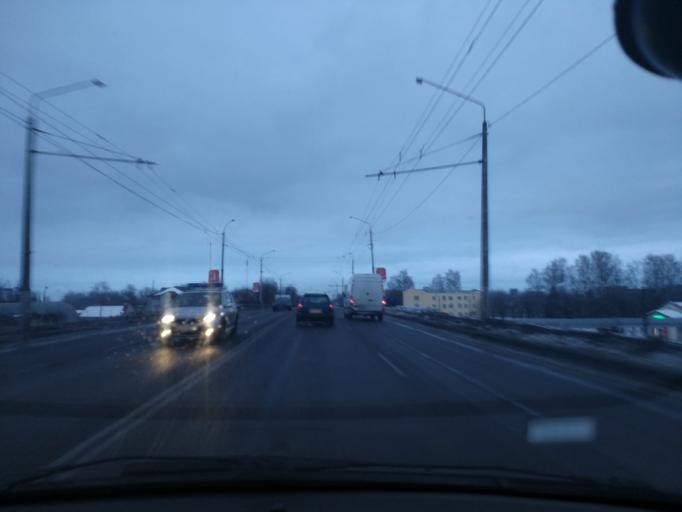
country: BY
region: Mogilev
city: Buynichy
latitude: 53.8906
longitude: 30.2900
